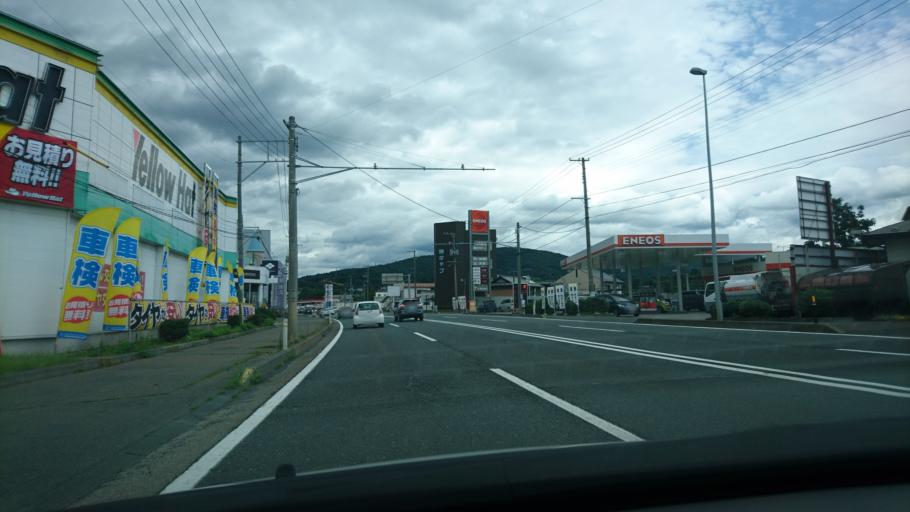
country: JP
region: Iwate
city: Morioka-shi
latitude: 39.6868
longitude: 141.1637
